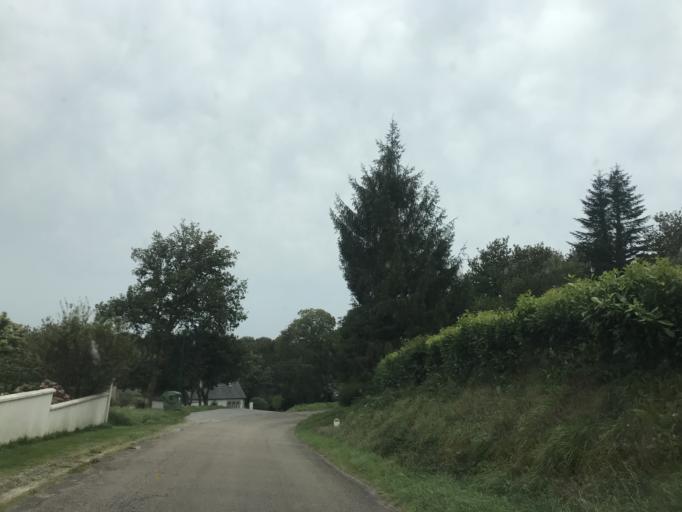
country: FR
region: Brittany
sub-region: Departement du Finistere
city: Plouneour-Menez
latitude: 48.3843
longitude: -3.9113
